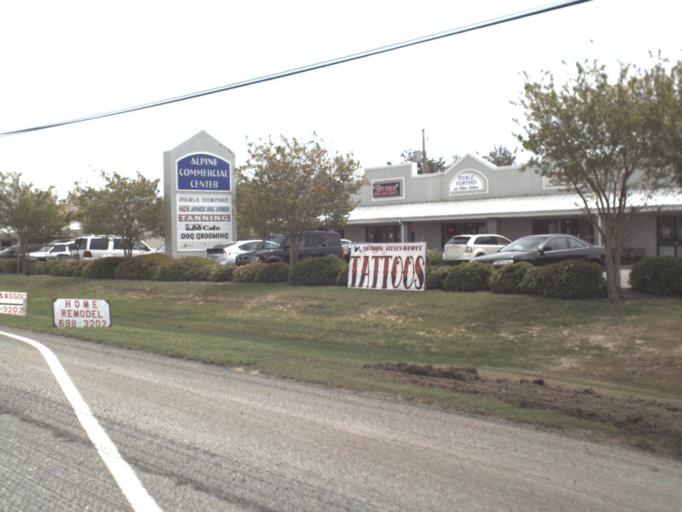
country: US
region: Florida
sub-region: Santa Rosa County
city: Navarre
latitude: 30.4016
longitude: -86.8861
